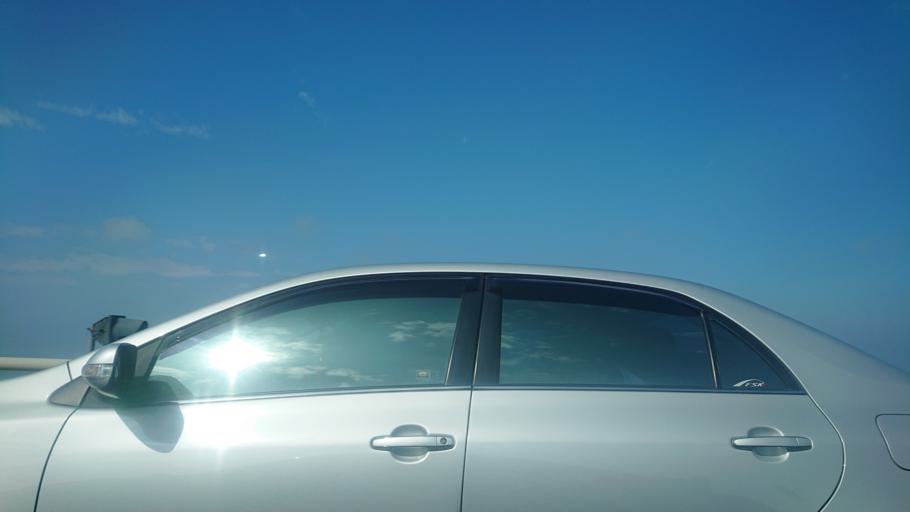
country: TW
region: Taiwan
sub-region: Changhua
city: Chang-hua
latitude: 24.0931
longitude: 120.4317
